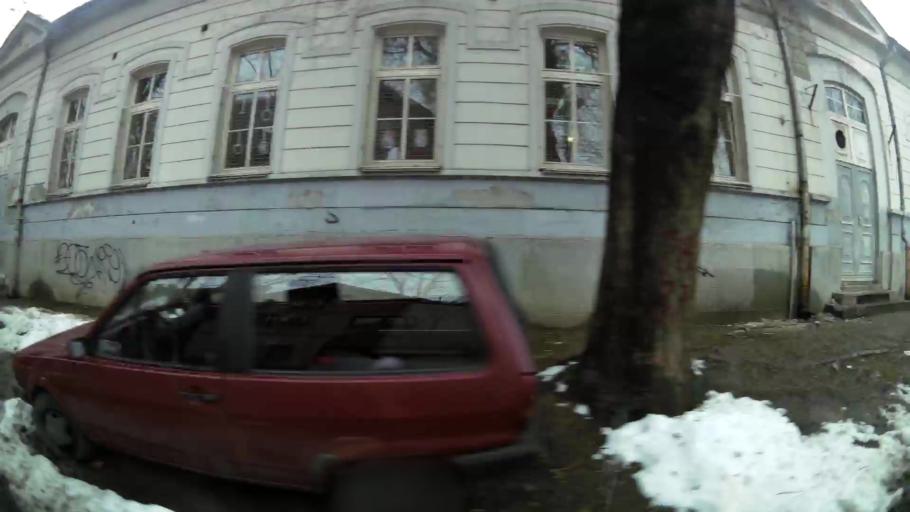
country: RS
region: Central Serbia
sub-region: Belgrade
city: Zemun
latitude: 44.8502
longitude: 20.3967
